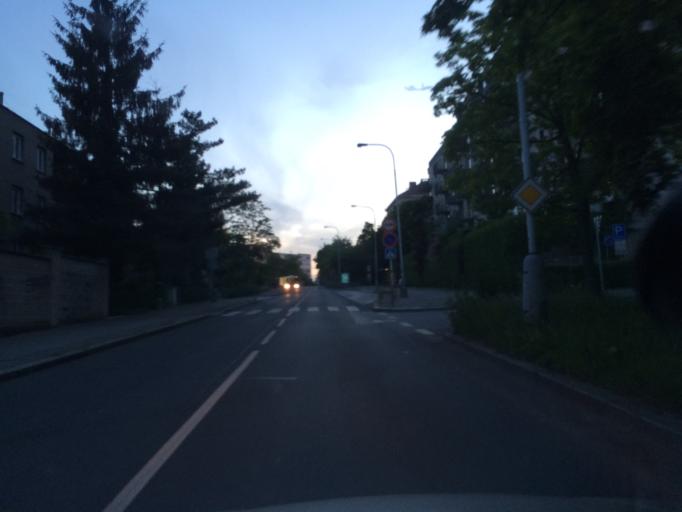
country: CZ
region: Praha
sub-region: Praha 4
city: Hodkovicky
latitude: 50.0426
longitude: 14.4584
